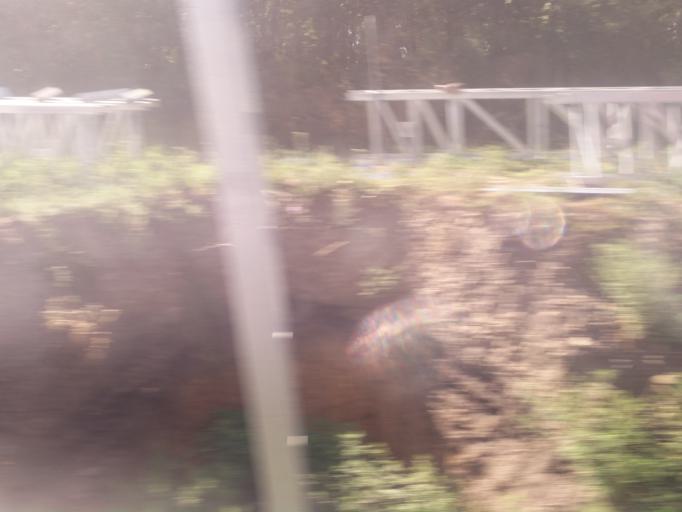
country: RU
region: Rostov
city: Gornyy
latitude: 47.8669
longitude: 40.1747
